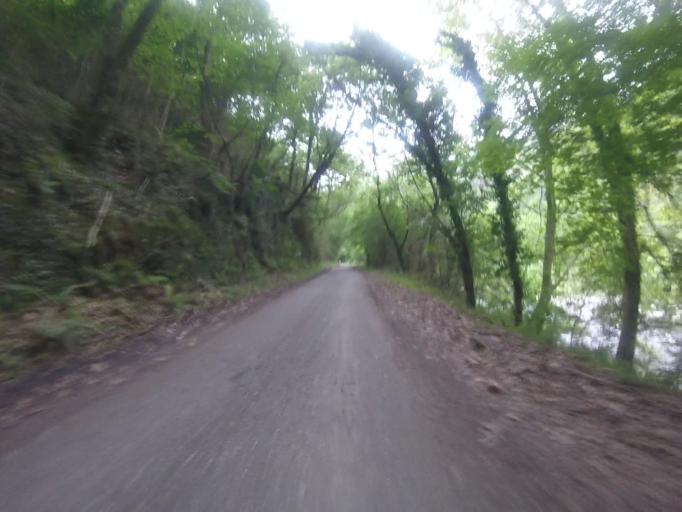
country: ES
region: Navarre
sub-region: Provincia de Navarra
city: Etxalar
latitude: 43.2062
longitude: -1.6623
